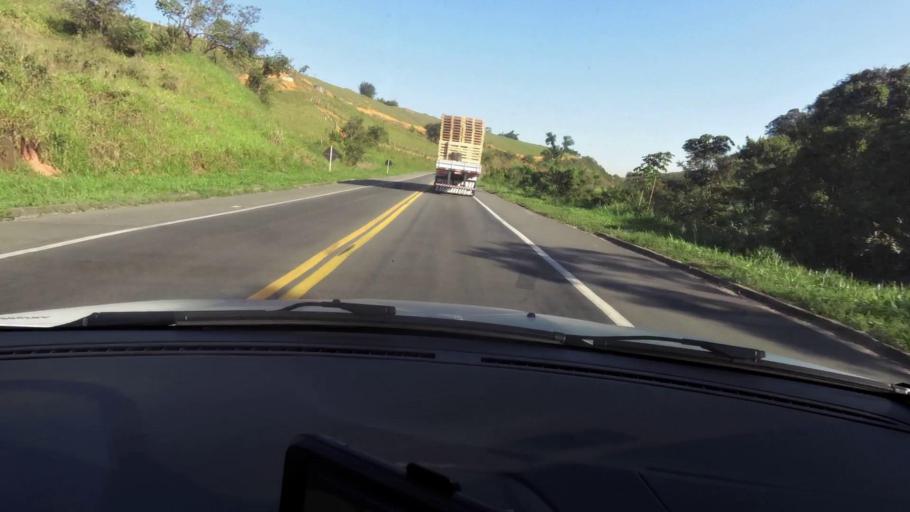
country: BR
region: Espirito Santo
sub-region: Alfredo Chaves
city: Alfredo Chaves
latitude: -20.6737
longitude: -40.6646
